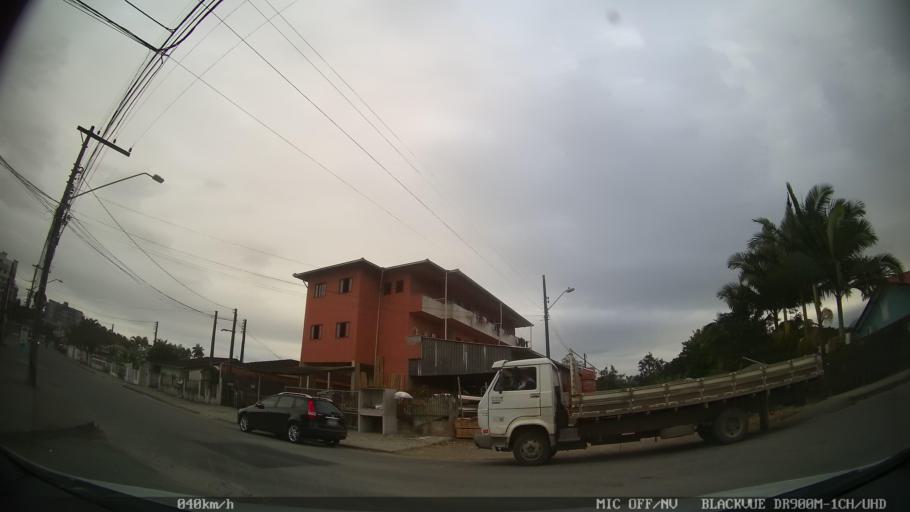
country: BR
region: Santa Catarina
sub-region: Joinville
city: Joinville
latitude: -26.2741
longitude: -48.8805
